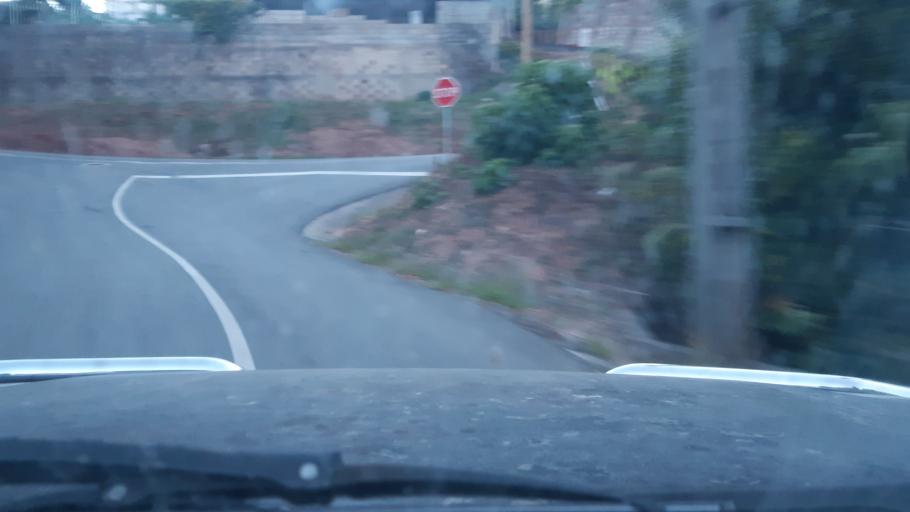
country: PT
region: Aveiro
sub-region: Agueda
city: Agueda
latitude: 40.5825
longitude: -8.4531
